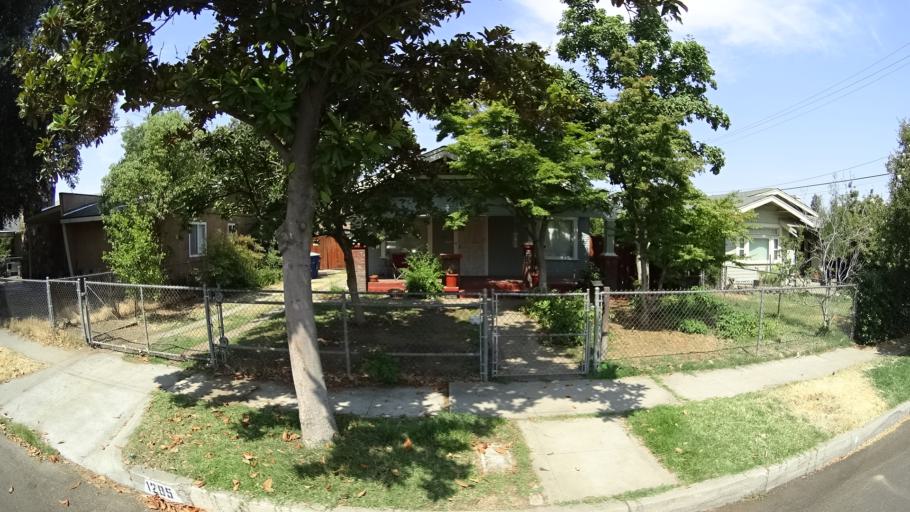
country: US
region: California
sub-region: Fresno County
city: Fresno
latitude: 36.7593
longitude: -119.7967
